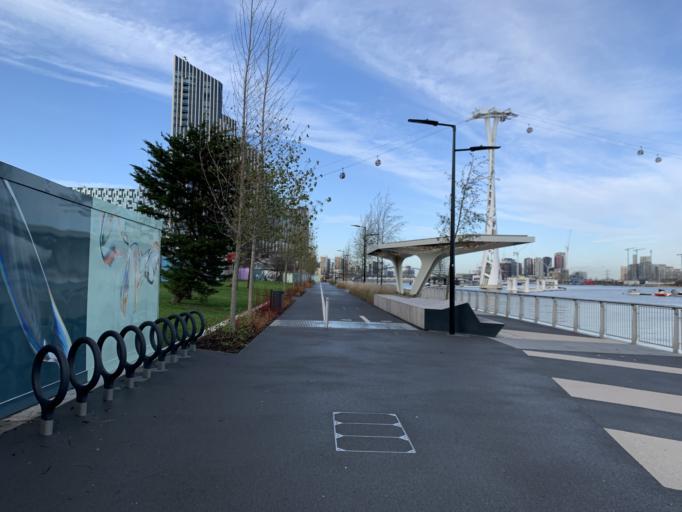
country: GB
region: England
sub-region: Greater London
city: Poplar
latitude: 51.4990
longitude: 0.0110
